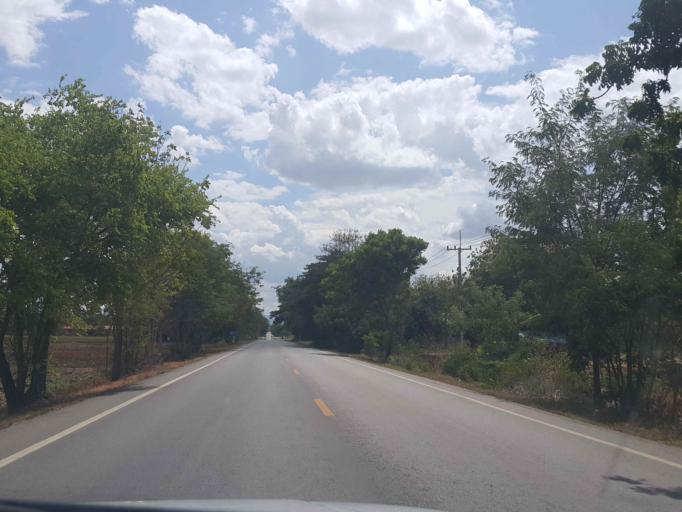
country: TH
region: Sukhothai
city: Thung Saliam
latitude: 17.3358
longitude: 99.5702
